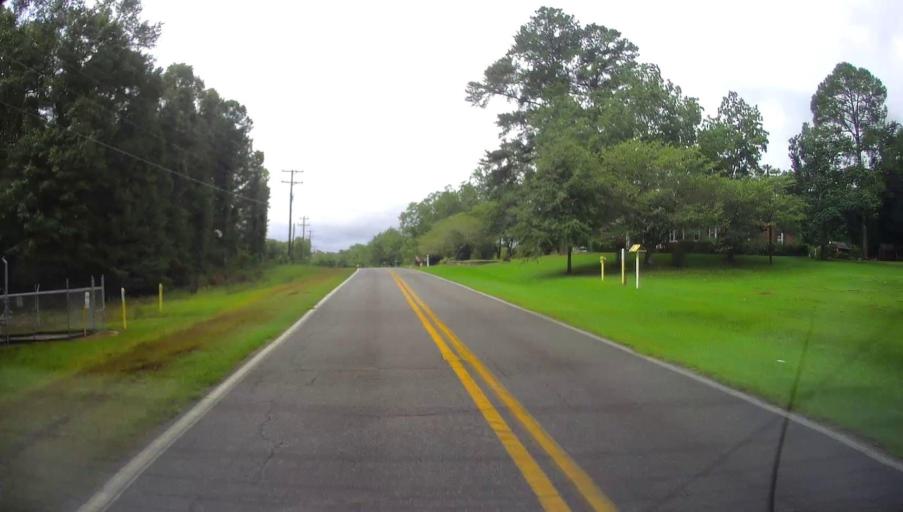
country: US
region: Georgia
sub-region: Bibb County
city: West Point
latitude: 32.7953
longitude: -83.8278
